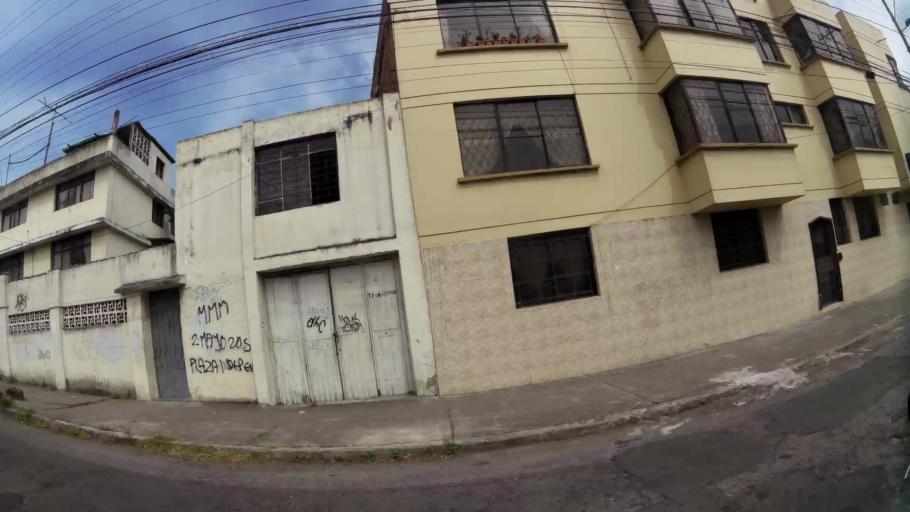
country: EC
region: Pichincha
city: Quito
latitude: -0.2143
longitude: -78.4866
